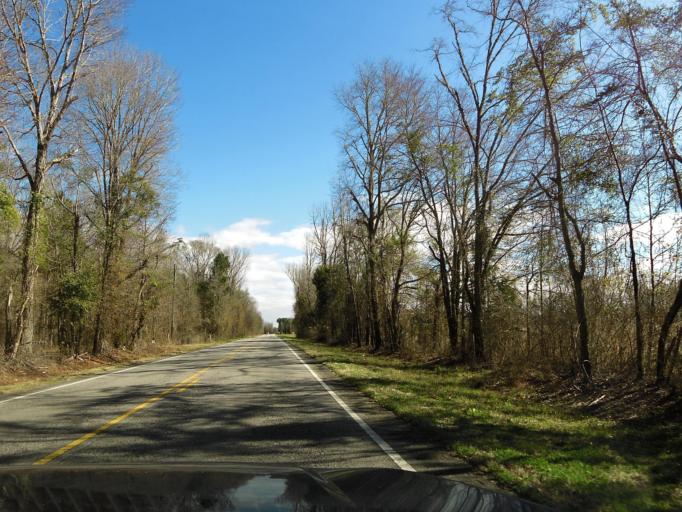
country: US
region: Alabama
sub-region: Barbour County
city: Clayton
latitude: 32.0262
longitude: -85.3367
